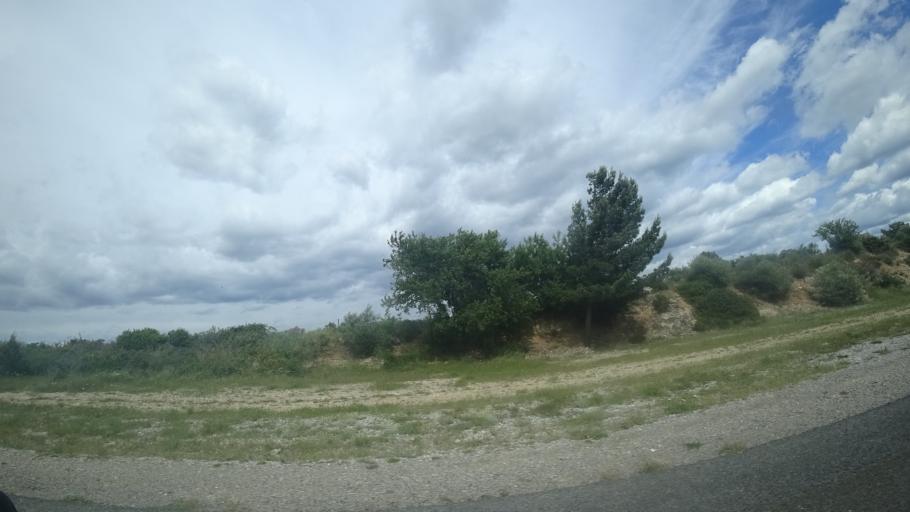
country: FR
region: Languedoc-Roussillon
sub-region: Departement de l'Aude
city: Leucate
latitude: 42.9179
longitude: 3.0205
